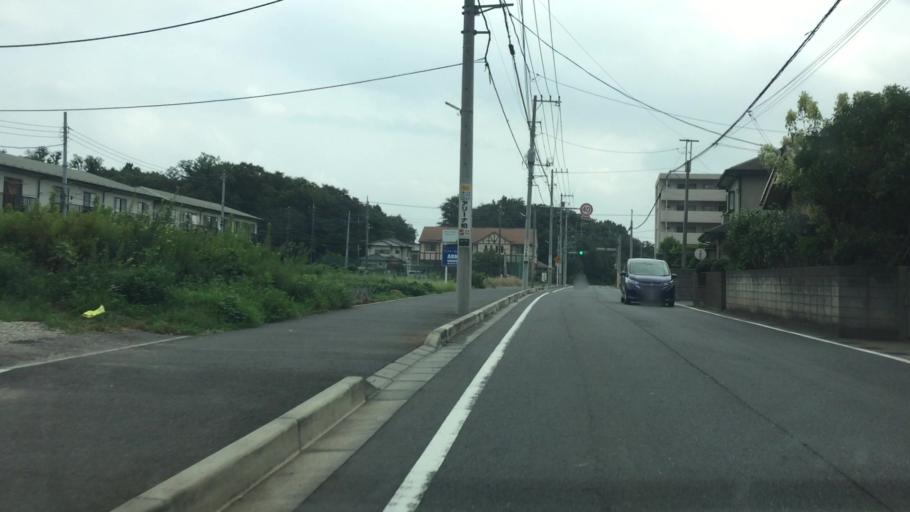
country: JP
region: Chiba
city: Kashiwa
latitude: 35.8091
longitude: 139.9505
